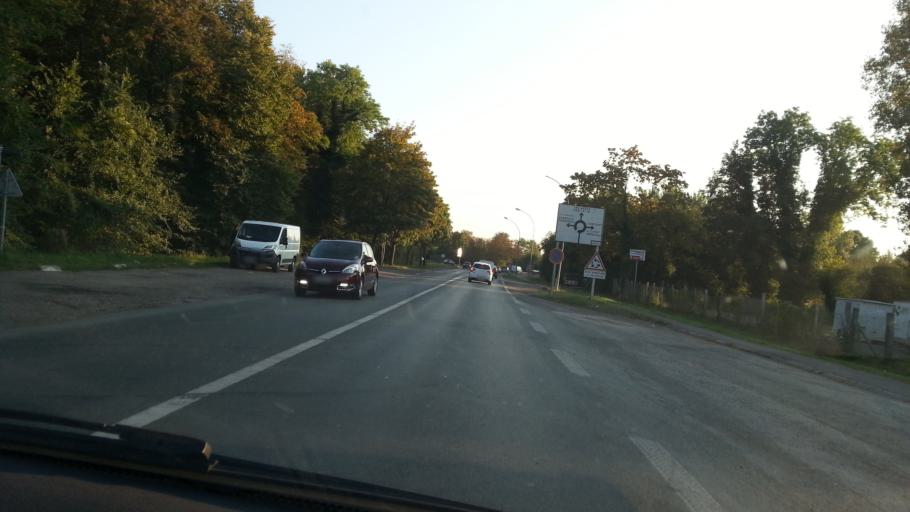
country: FR
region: Picardie
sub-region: Departement de l'Oise
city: Les Ageux
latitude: 49.3267
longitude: 2.6033
